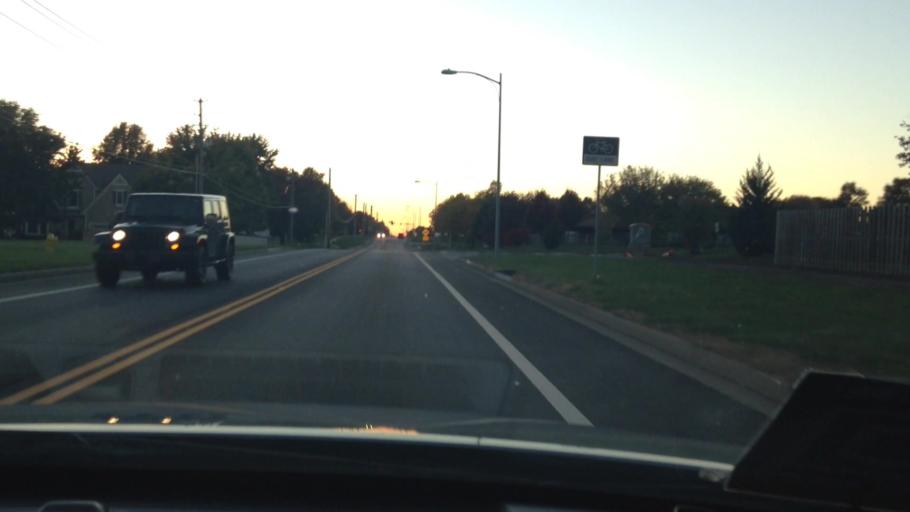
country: US
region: Kansas
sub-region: Johnson County
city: Olathe
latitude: 38.8691
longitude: -94.7563
